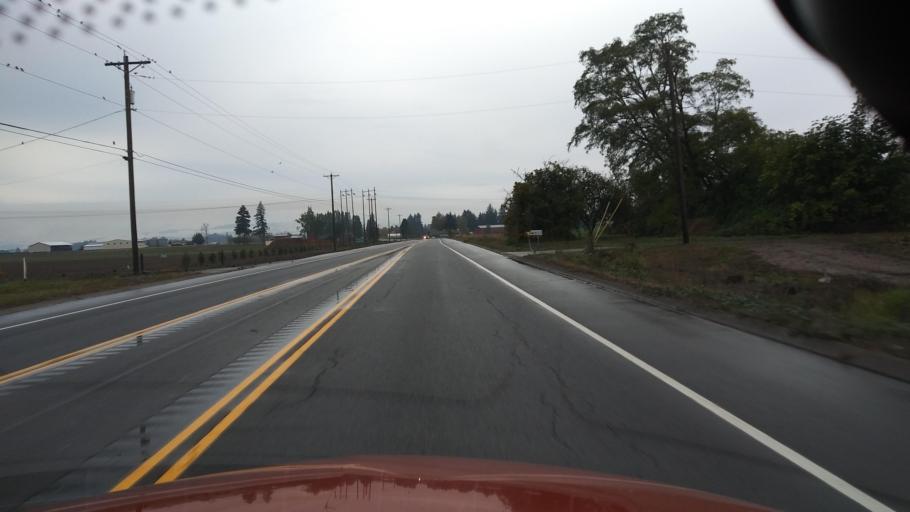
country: US
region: Oregon
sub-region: Washington County
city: Cornelius
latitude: 45.5417
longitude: -123.0596
